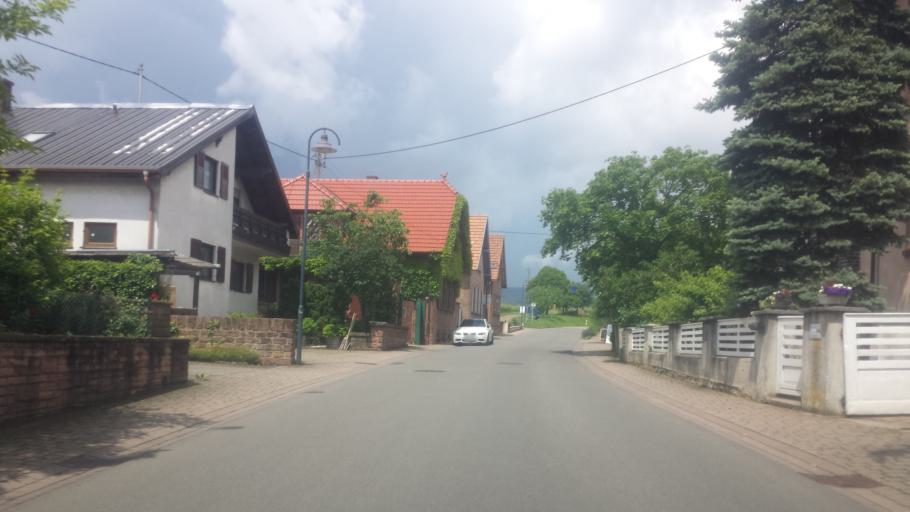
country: DE
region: Rheinland-Pfalz
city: Hainfeld
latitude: 49.2592
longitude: 8.1018
